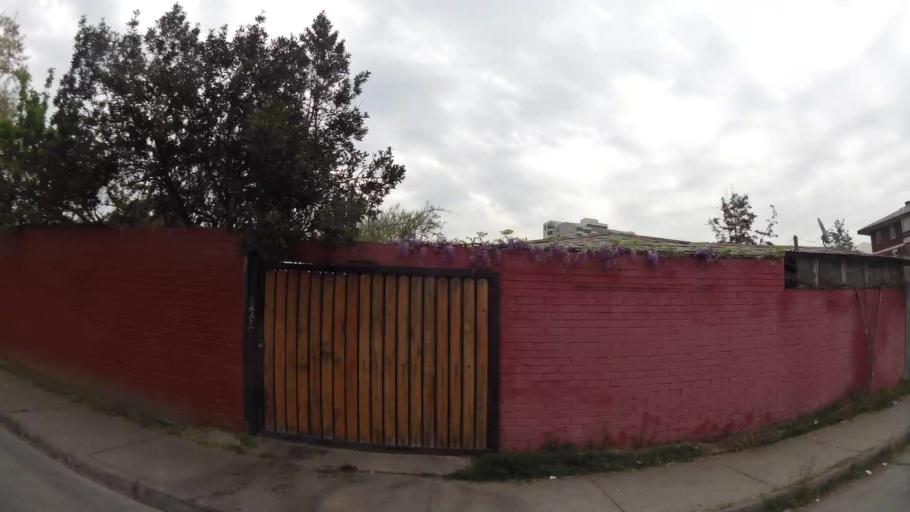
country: CL
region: Santiago Metropolitan
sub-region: Provincia de Santiago
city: Villa Presidente Frei, Nunoa, Santiago, Chile
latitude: -33.5133
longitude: -70.6047
